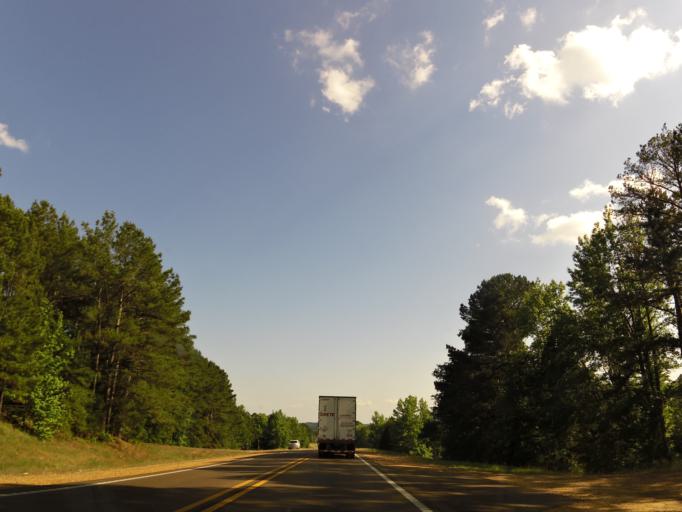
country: US
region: Mississippi
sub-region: Lafayette County
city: University
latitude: 34.2897
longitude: -89.5203
